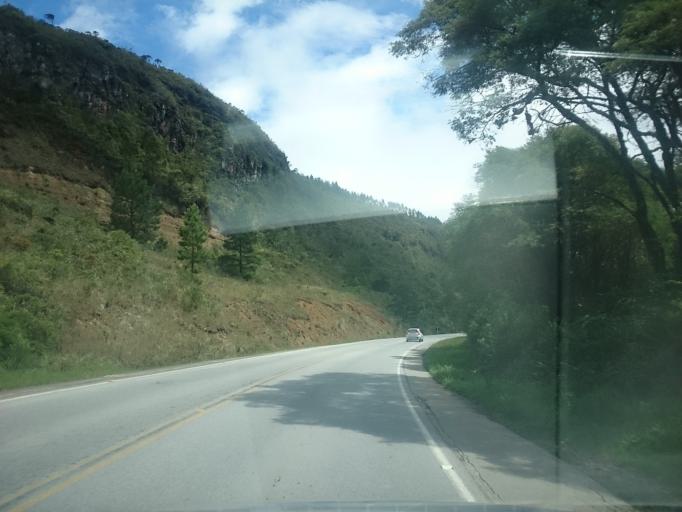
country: BR
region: Santa Catarina
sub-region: Anitapolis
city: Anitapolis
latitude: -27.6896
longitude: -49.1213
